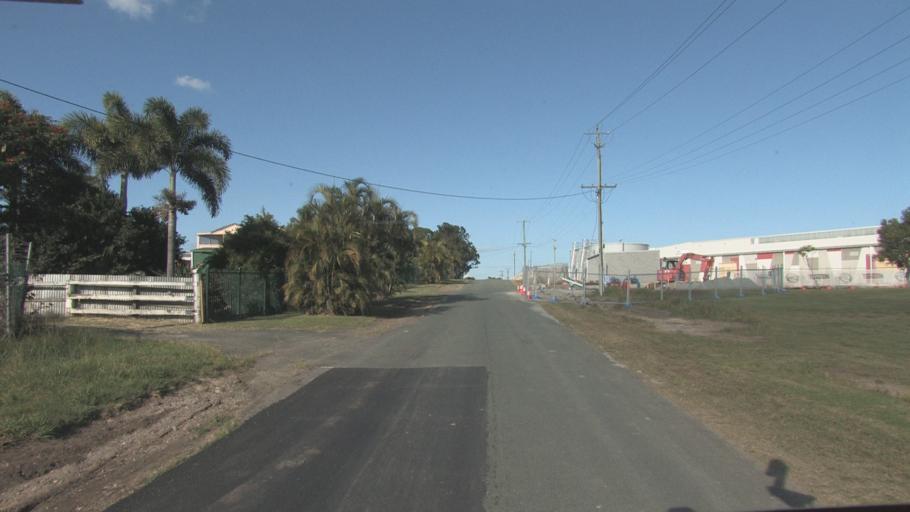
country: AU
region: Queensland
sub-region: Gold Coast
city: Yatala
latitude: -27.7220
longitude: 153.2192
